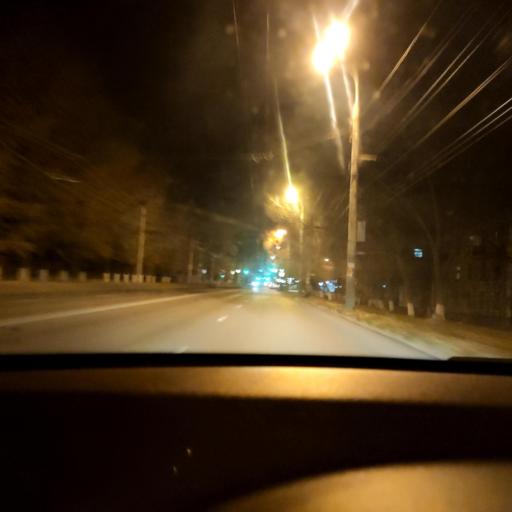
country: RU
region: Samara
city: Samara
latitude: 53.2328
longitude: 50.2458
